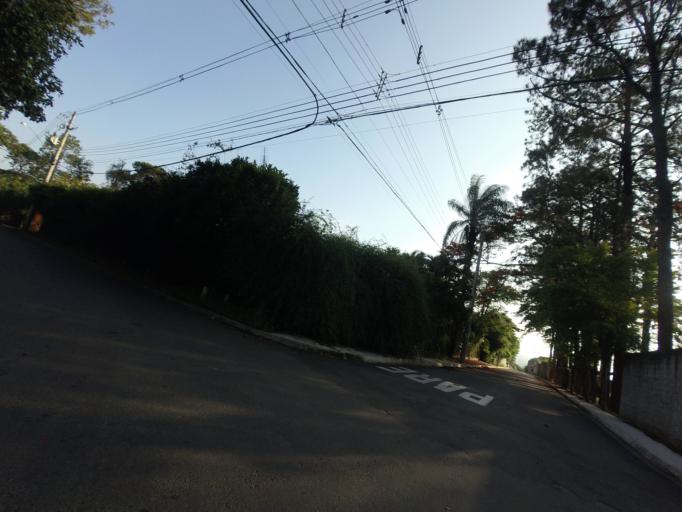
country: BR
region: Sao Paulo
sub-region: Piracicaba
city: Piracicaba
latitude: -22.7456
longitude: -47.6073
